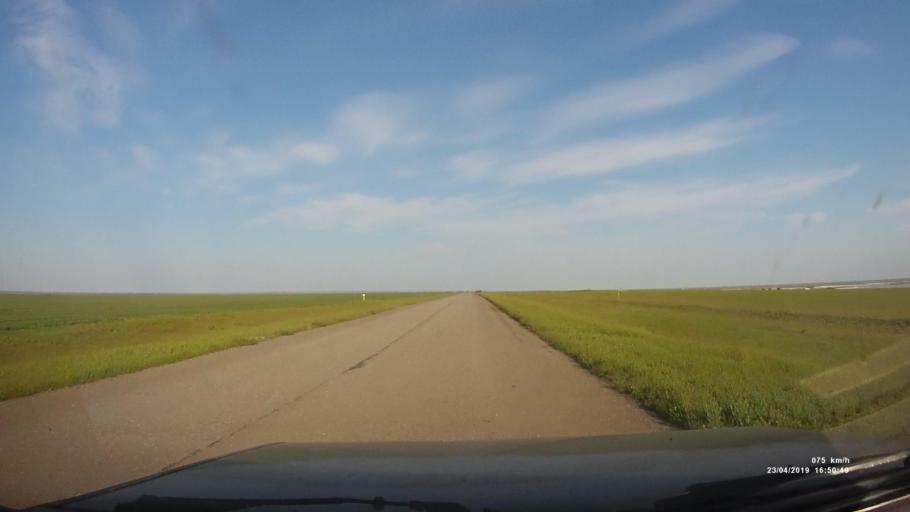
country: RU
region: Kalmykiya
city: Priyutnoye
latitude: 46.3252
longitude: 43.2982
